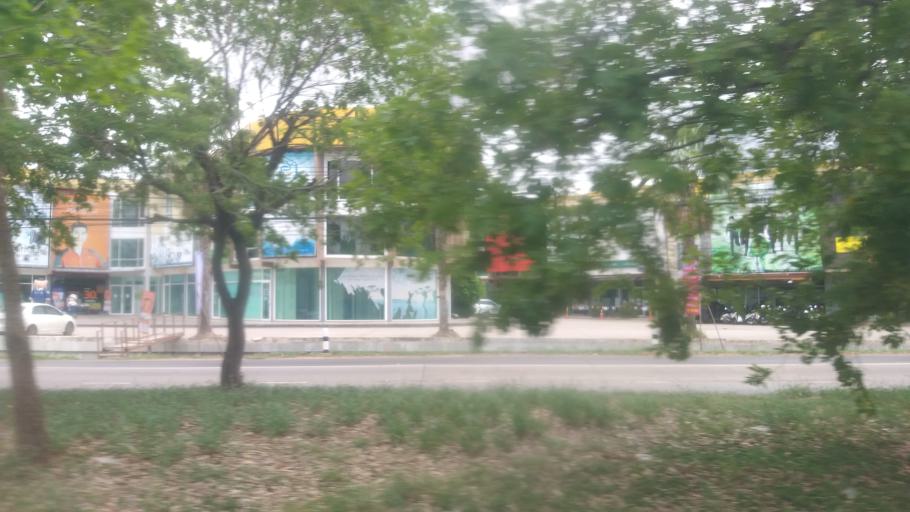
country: TH
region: Nakhon Ratchasima
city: Nakhon Ratchasima
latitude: 15.0462
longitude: 102.1330
